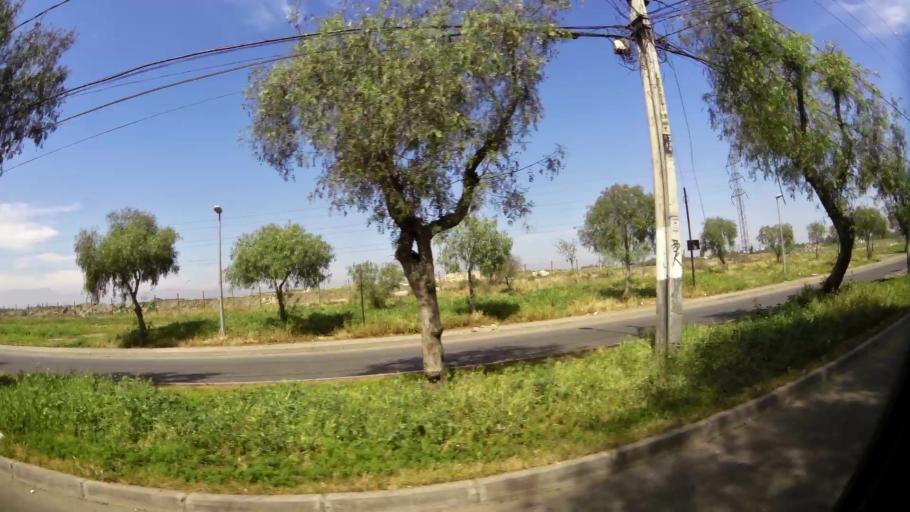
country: CL
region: Santiago Metropolitan
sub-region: Provincia de Santiago
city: Lo Prado
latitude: -33.4815
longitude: -70.7207
